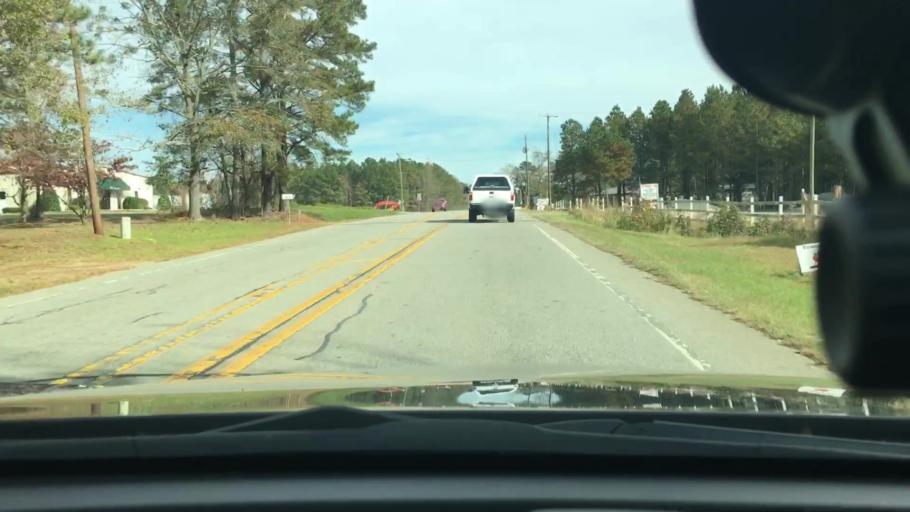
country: US
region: North Carolina
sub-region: Moore County
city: Carthage
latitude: 35.3772
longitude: -79.2907
